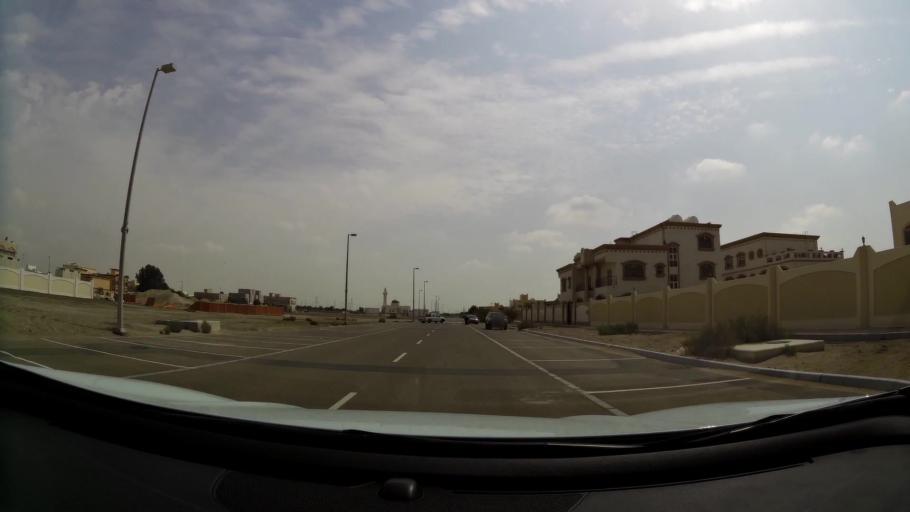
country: AE
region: Abu Dhabi
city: Abu Dhabi
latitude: 24.5559
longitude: 54.6368
